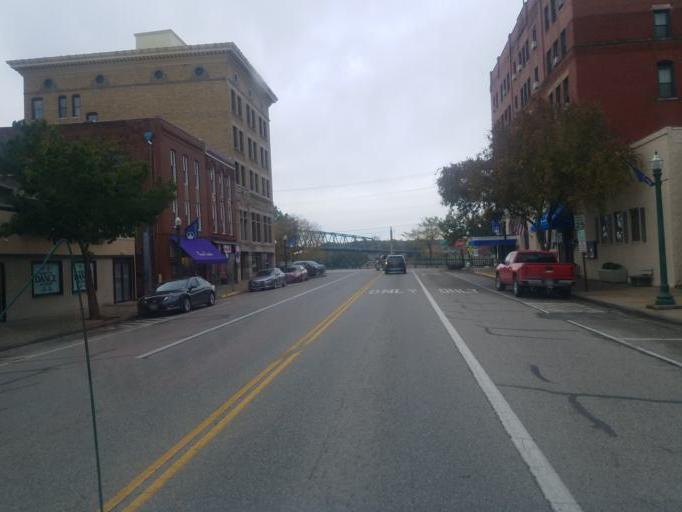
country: US
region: Ohio
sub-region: Washington County
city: Marietta
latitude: 39.4112
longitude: -81.4527
